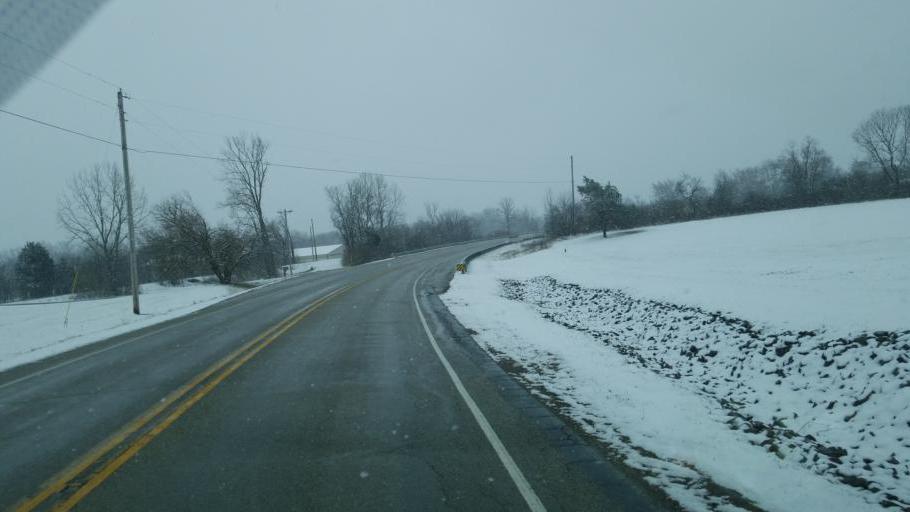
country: US
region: Indiana
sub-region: Wayne County
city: Richmond
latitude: 39.9168
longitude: -84.9527
